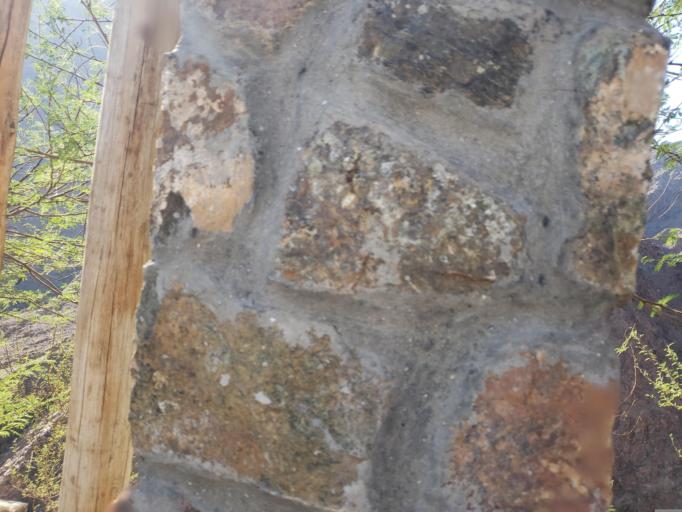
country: AE
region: Ash Shariqah
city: Khawr Fakkan
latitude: 25.2926
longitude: 56.2358
